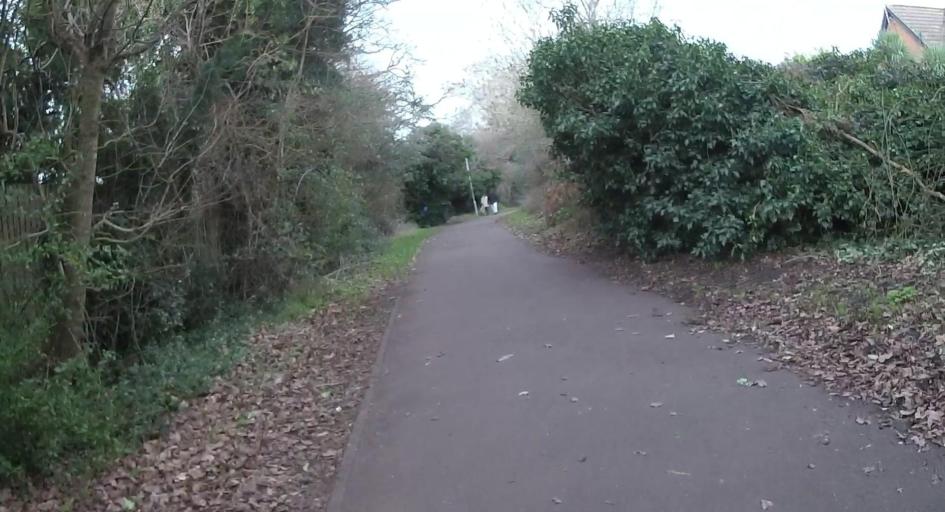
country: GB
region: England
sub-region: Wokingham
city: Wokingham
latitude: 51.4120
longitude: -0.8558
